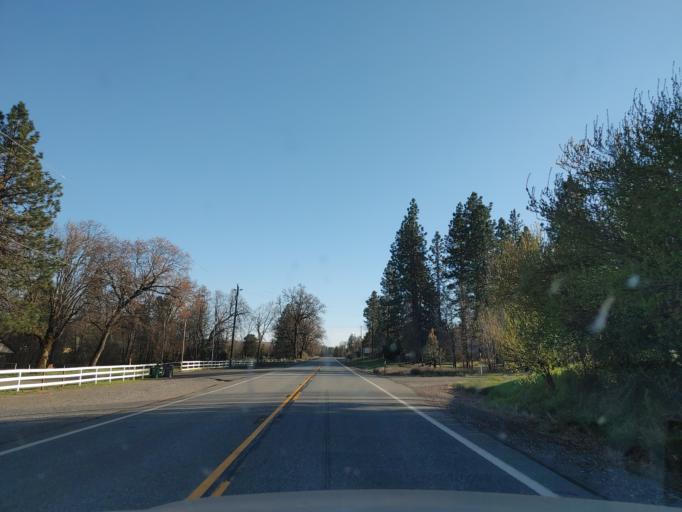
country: US
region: California
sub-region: Shasta County
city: Burney
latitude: 40.8116
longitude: -121.9392
